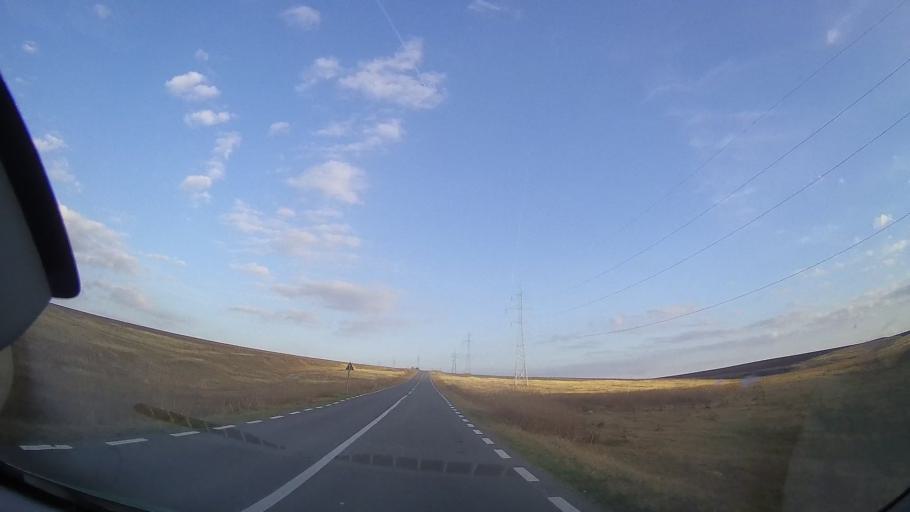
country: RO
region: Constanta
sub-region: Comuna Chirnogeni
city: Plopeni
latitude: 43.9538
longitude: 28.1519
